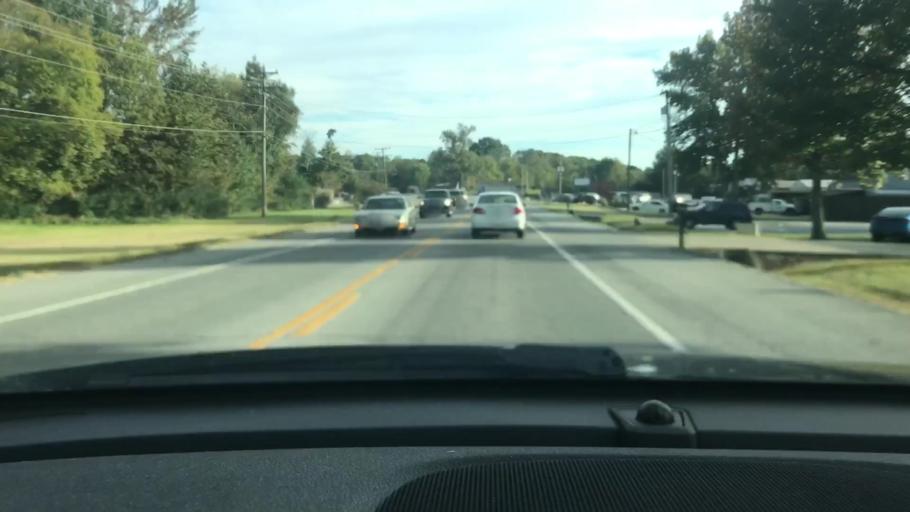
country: US
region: Tennessee
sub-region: Sumner County
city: Millersville
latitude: 36.4119
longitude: -86.6921
